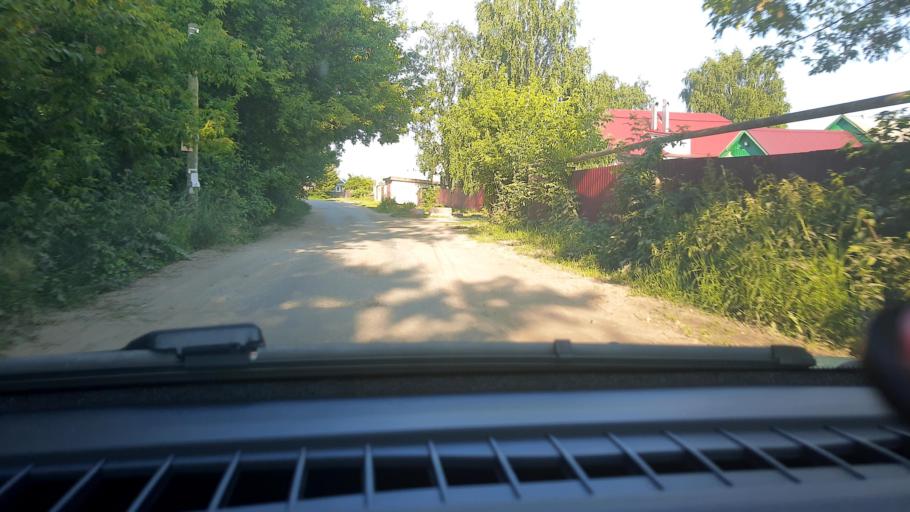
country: RU
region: Nizjnij Novgorod
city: Nizhniy Novgorod
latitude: 56.1874
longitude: 43.9407
